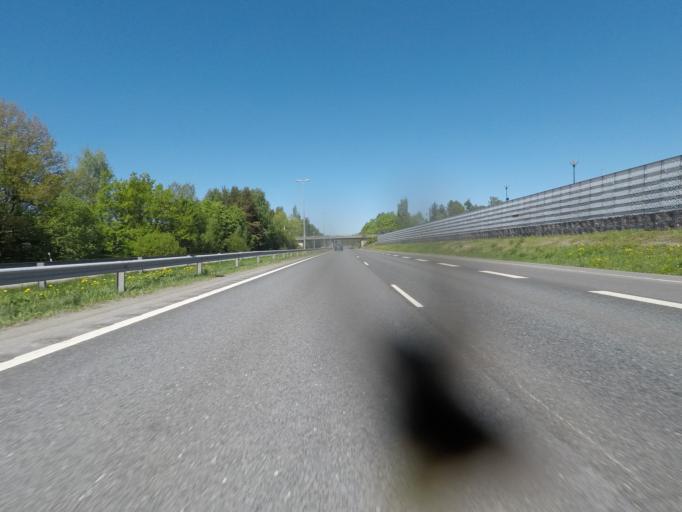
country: FI
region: Haeme
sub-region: Haemeenlinna
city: Haemeenlinna
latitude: 60.9951
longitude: 24.4553
